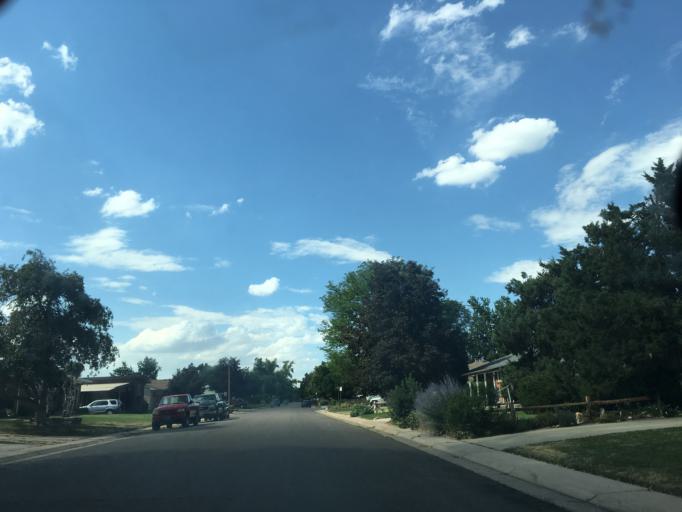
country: US
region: Colorado
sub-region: Arapahoe County
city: Sheridan
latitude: 39.6866
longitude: -105.0401
